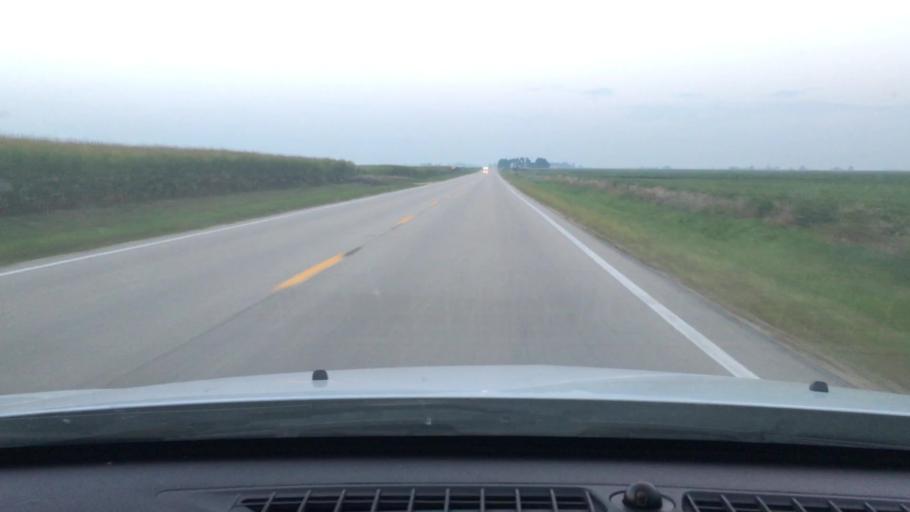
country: US
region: Illinois
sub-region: Ogle County
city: Rochelle
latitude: 41.8769
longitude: -89.0731
